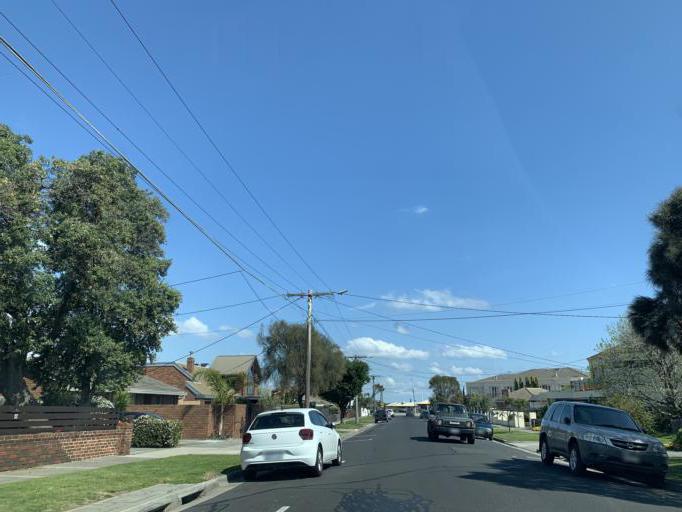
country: AU
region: Victoria
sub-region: Kingston
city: Parkdale
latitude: -37.9982
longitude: 145.0759
